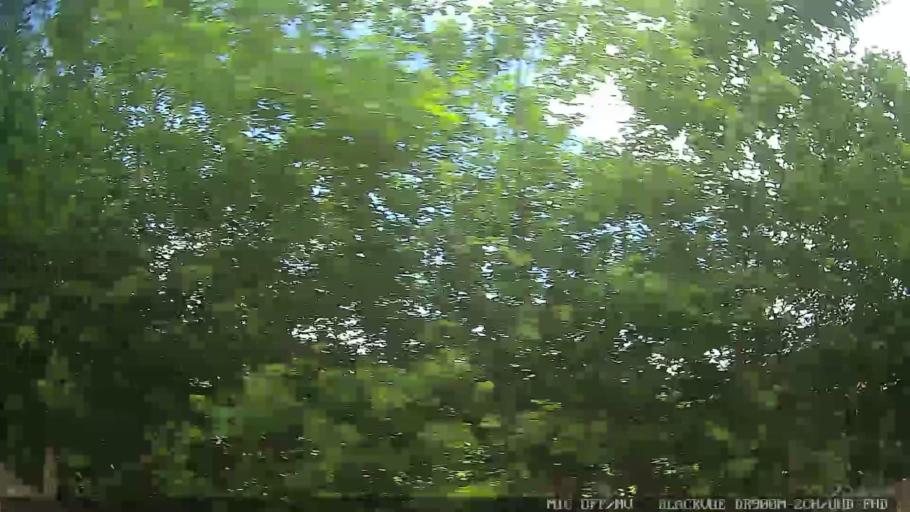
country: BR
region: Sao Paulo
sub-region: Conchas
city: Conchas
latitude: -22.9824
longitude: -47.9902
